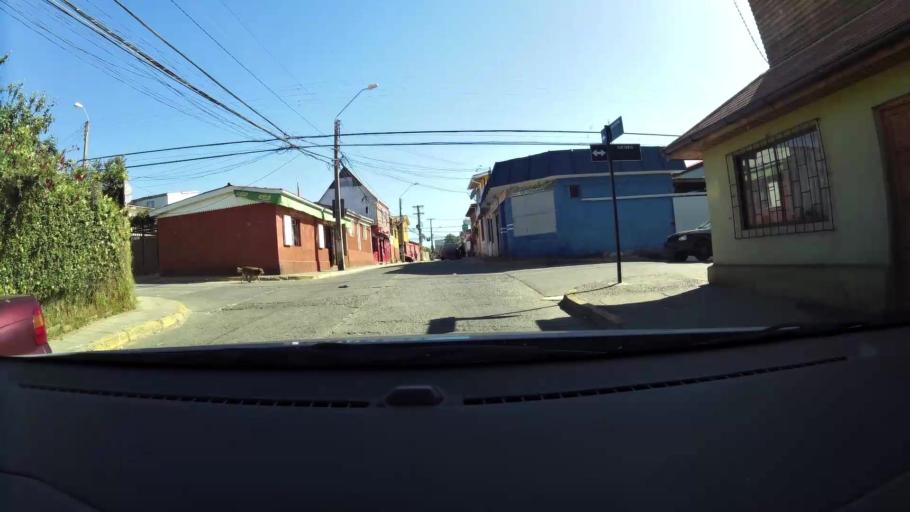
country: CL
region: Valparaiso
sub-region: Provincia de Valparaiso
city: Vina del Mar
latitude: -33.0468
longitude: -71.5631
